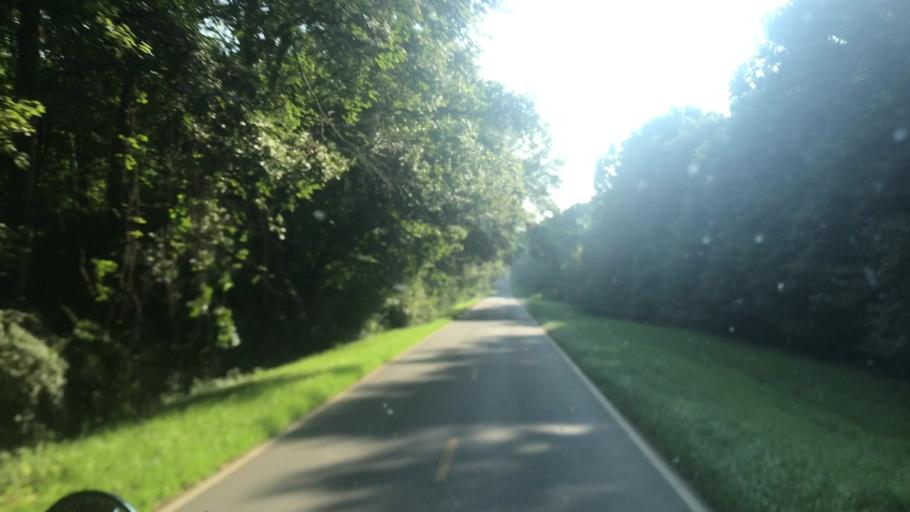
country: US
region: Florida
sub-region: Gadsden County
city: Quincy
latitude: 30.6674
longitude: -84.5512
